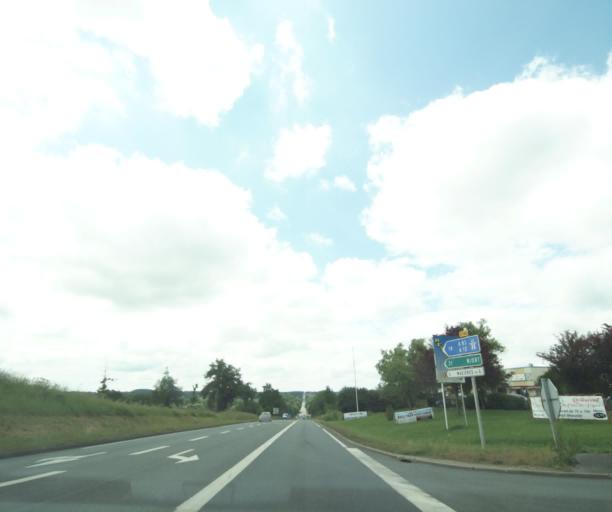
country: FR
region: Poitou-Charentes
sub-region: Departement des Deux-Sevres
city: Saint-Pardoux
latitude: 46.5693
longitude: -0.2983
